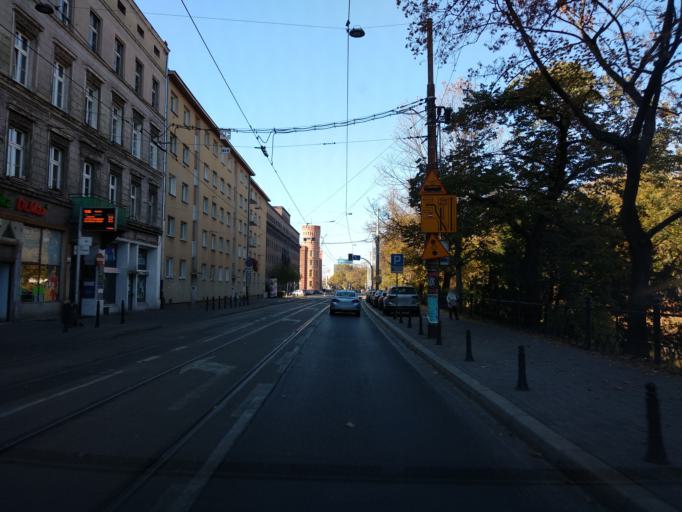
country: PL
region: Lower Silesian Voivodeship
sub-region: Powiat wroclawski
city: Wroclaw
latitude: 51.1044
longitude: 17.0300
